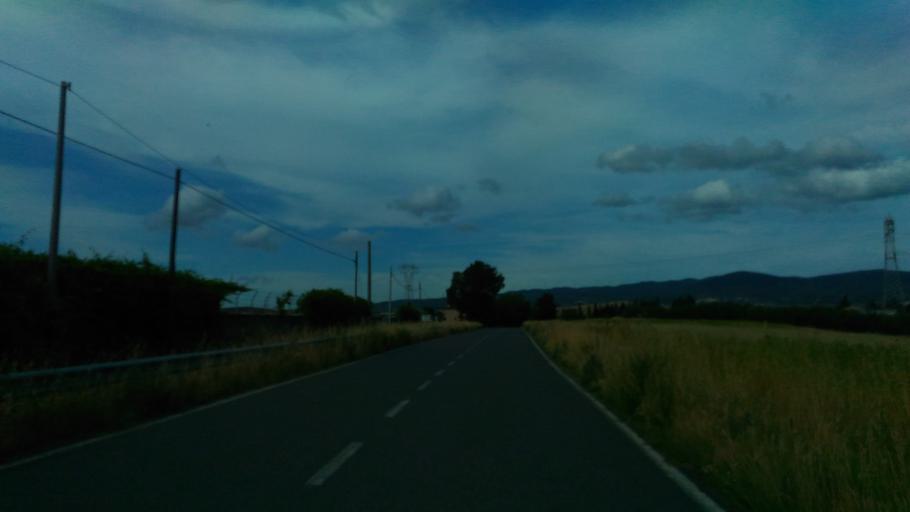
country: IT
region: Tuscany
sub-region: Provincia di Livorno
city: Rosignano Marittimo
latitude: 43.4394
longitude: 10.4938
